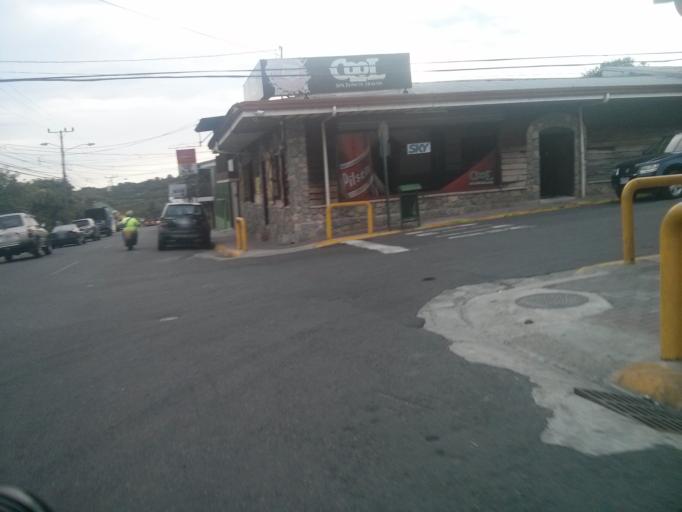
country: CR
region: Heredia
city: Angeles
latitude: 10.0179
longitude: -84.0554
